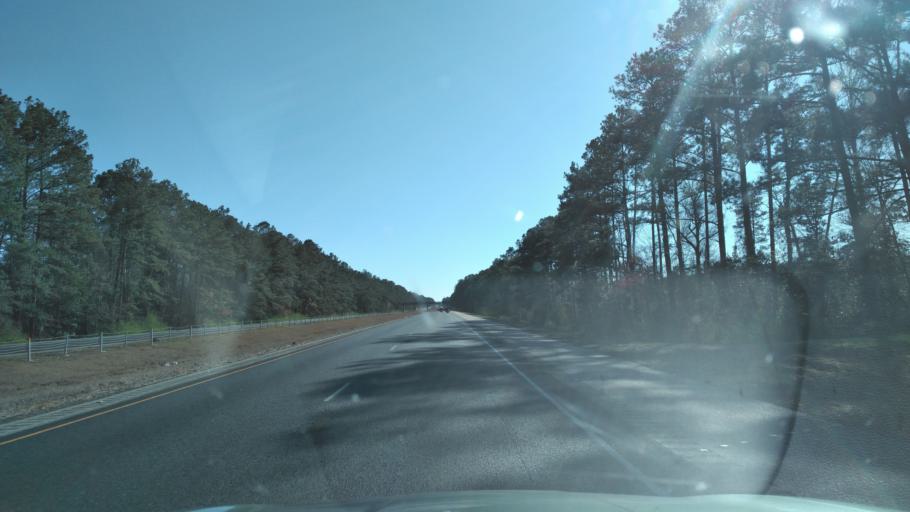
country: US
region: Alabama
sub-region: Butler County
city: Georgiana
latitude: 31.7322
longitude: -86.7195
